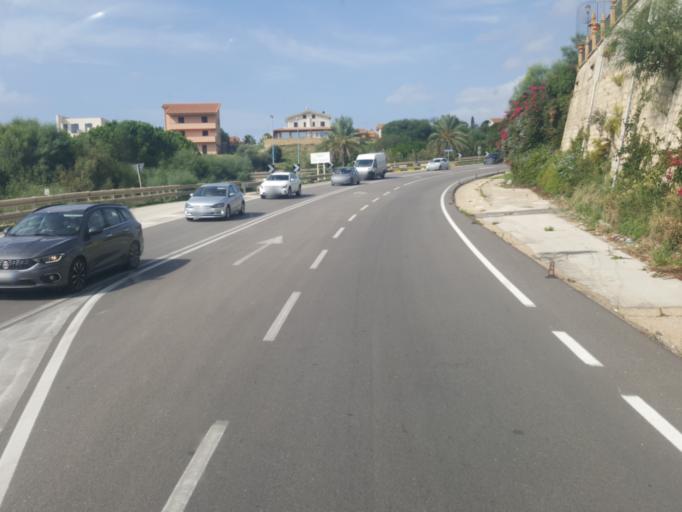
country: IT
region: Sicily
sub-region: Agrigento
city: Porto Empedocle
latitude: 37.2941
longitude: 13.4987
